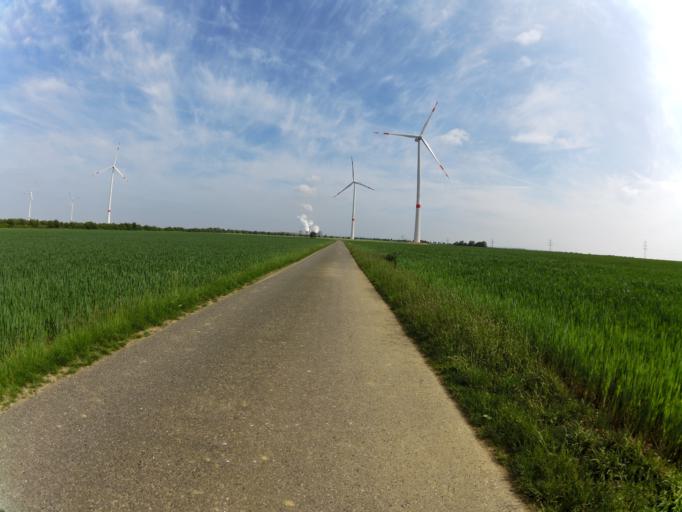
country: DE
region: North Rhine-Westphalia
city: Neu-Pattern
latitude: 50.8775
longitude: 6.2792
